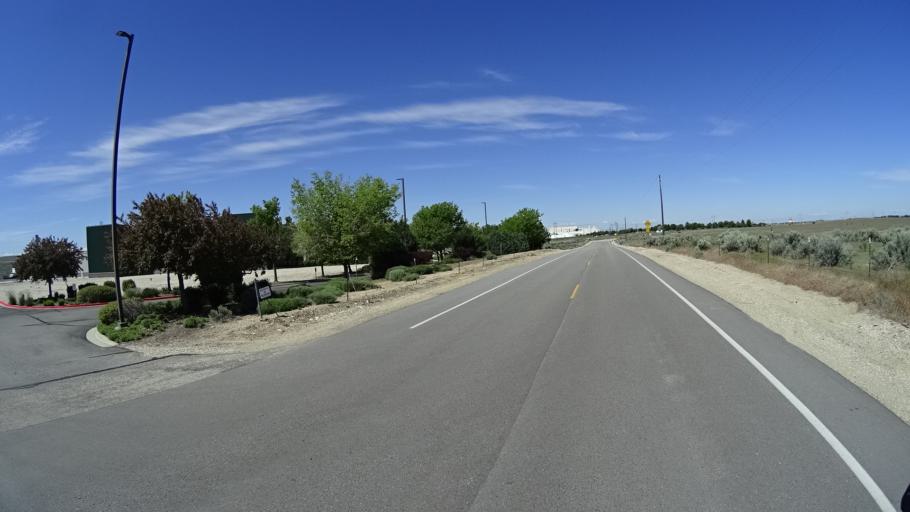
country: US
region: Idaho
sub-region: Ada County
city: Boise
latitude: 43.5312
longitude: -116.1343
